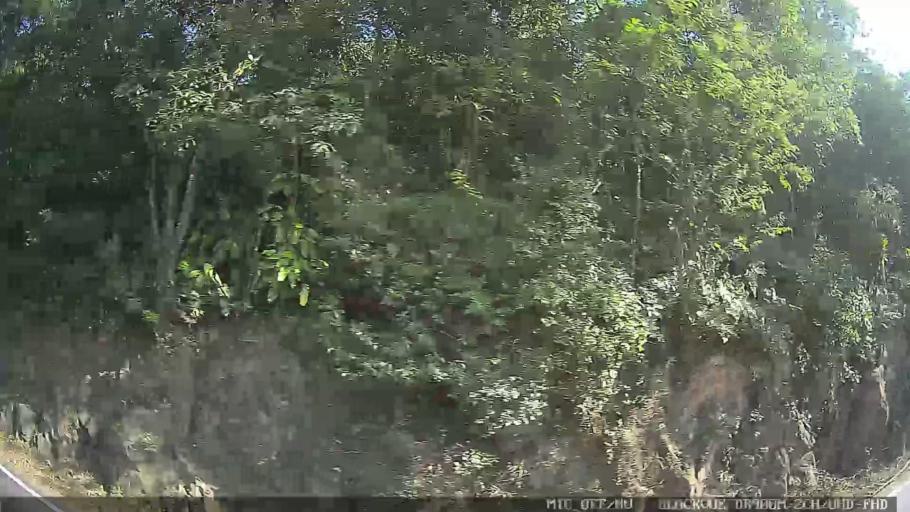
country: BR
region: Sao Paulo
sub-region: Cubatao
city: Cubatao
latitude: -23.8897
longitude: -46.4804
